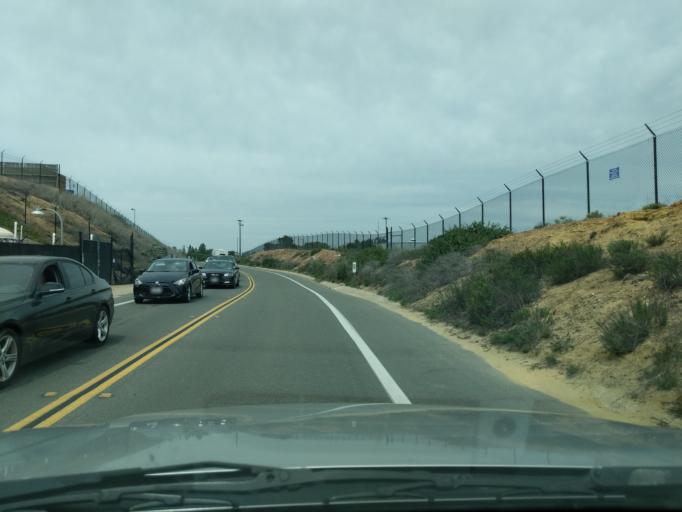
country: US
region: California
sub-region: San Diego County
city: Coronado
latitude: 32.6786
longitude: -117.2433
